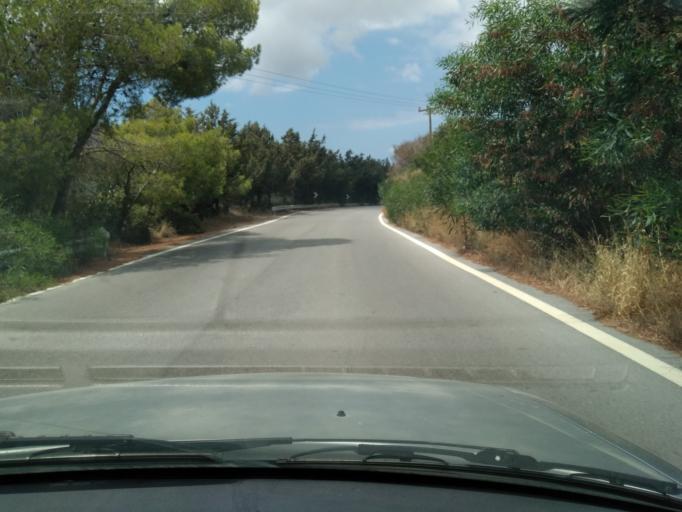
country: GR
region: Crete
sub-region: Nomos Lasithiou
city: Makry-Gialos
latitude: 35.0622
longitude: 26.0437
